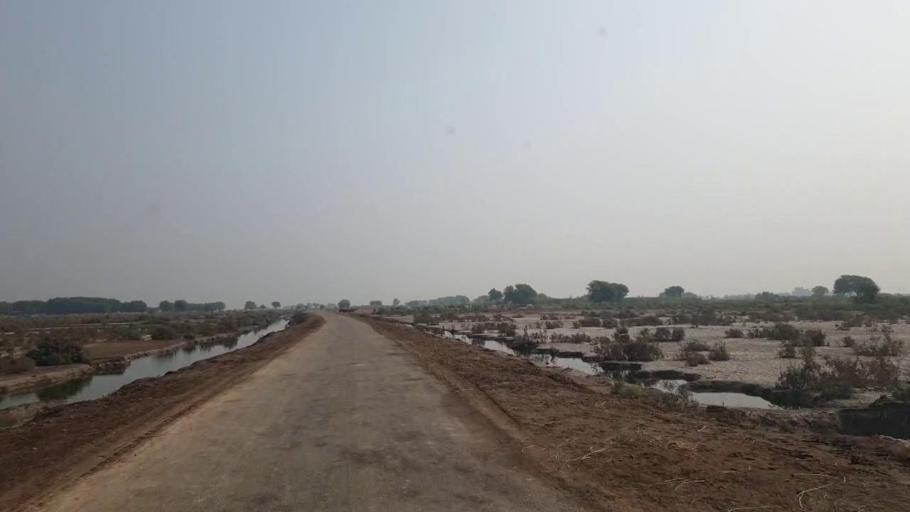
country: PK
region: Sindh
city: Matli
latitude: 25.1304
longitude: 68.6948
